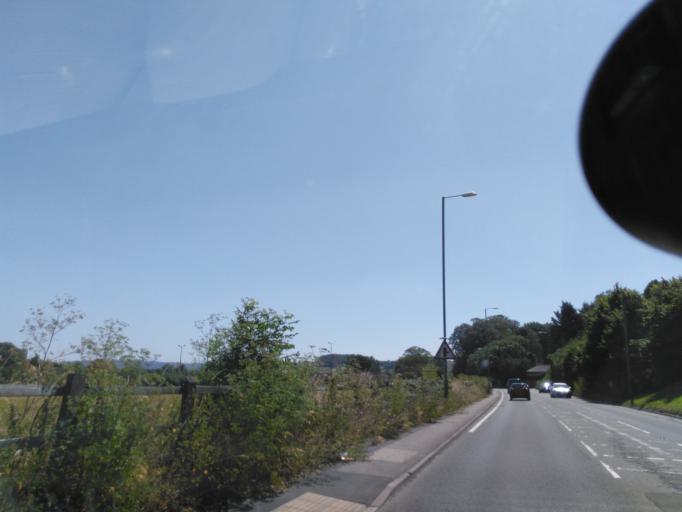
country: GB
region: England
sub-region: Bath and North East Somerset
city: Corston
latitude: 51.3919
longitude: -2.4402
